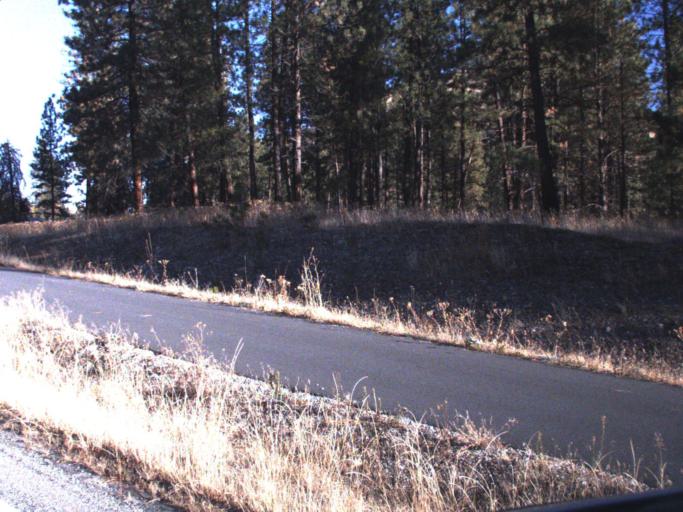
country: US
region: Washington
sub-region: Okanogan County
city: Coulee Dam
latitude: 48.0733
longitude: -118.6781
